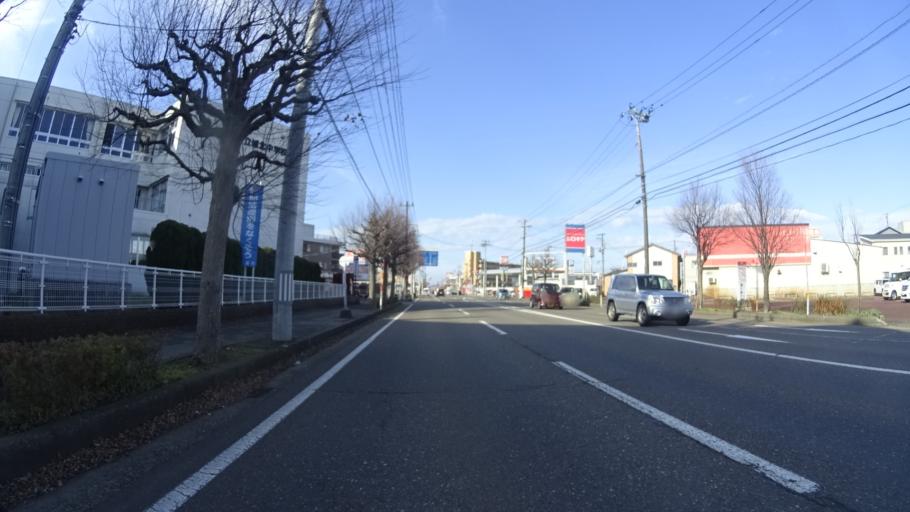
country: JP
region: Niigata
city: Joetsu
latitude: 37.1237
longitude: 138.2508
